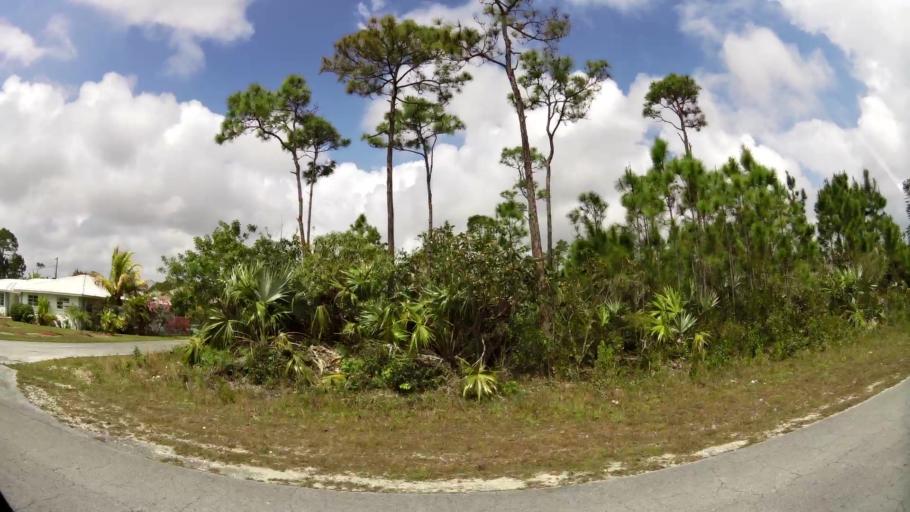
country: BS
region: Freeport
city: Lucaya
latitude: 26.5278
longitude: -78.6515
